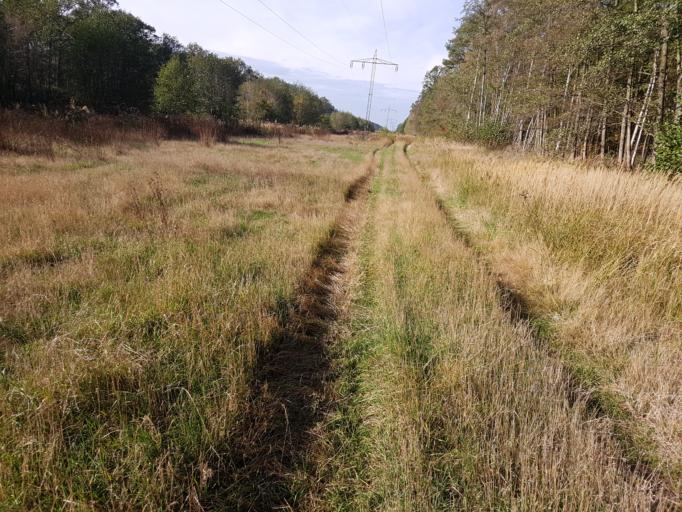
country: DE
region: Brandenburg
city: Schilda
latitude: 51.5894
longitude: 13.3435
